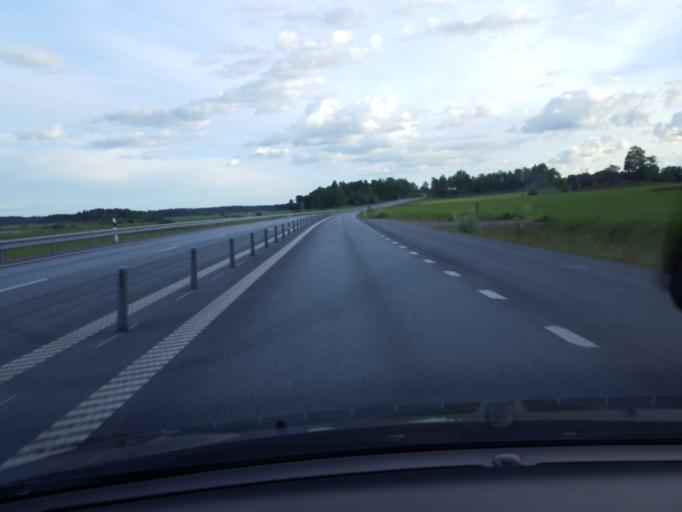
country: SE
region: Uppsala
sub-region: Osthammars Kommun
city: Gimo
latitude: 60.0437
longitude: 18.0440
